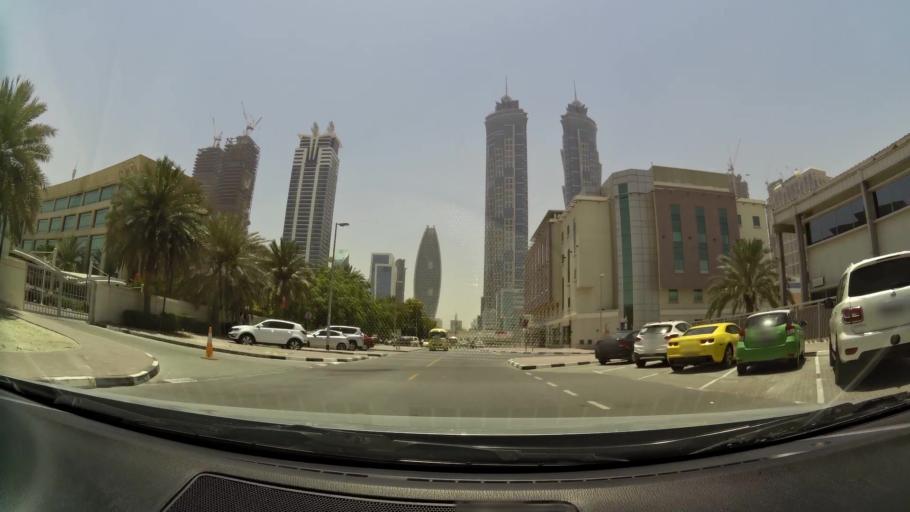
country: AE
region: Dubai
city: Dubai
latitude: 25.1893
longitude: 55.2547
